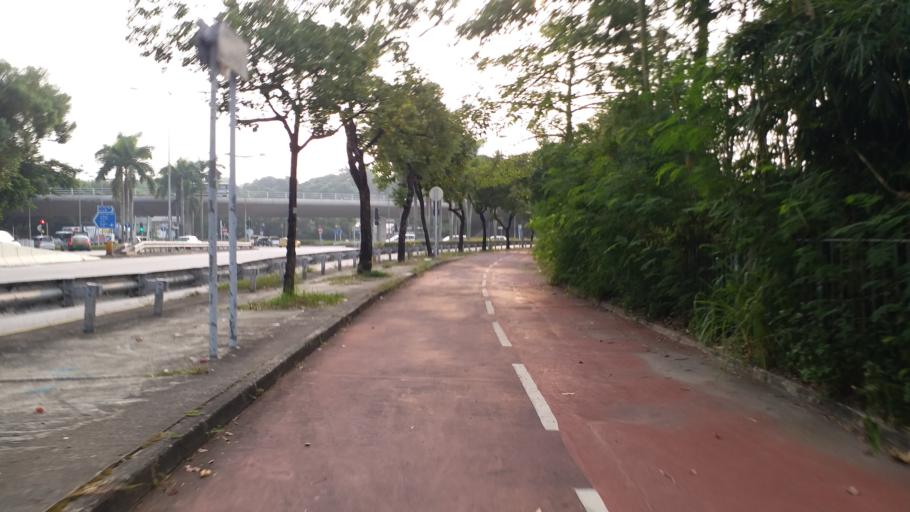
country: HK
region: Yuen Long
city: Yuen Long Kau Hui
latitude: 22.4474
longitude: 114.0168
